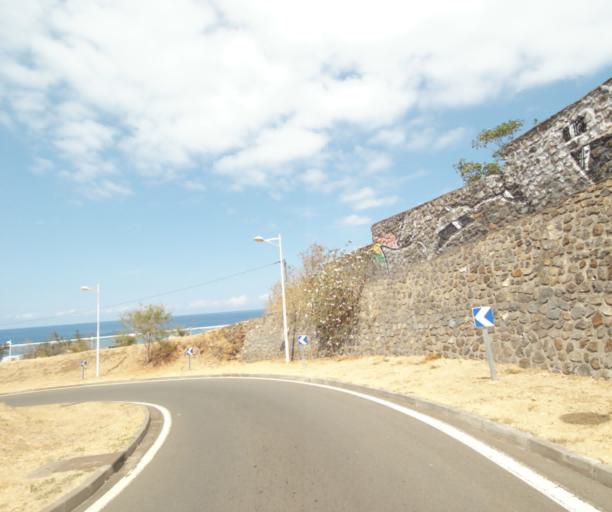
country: RE
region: Reunion
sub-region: Reunion
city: Trois-Bassins
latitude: -21.1023
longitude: 55.2474
